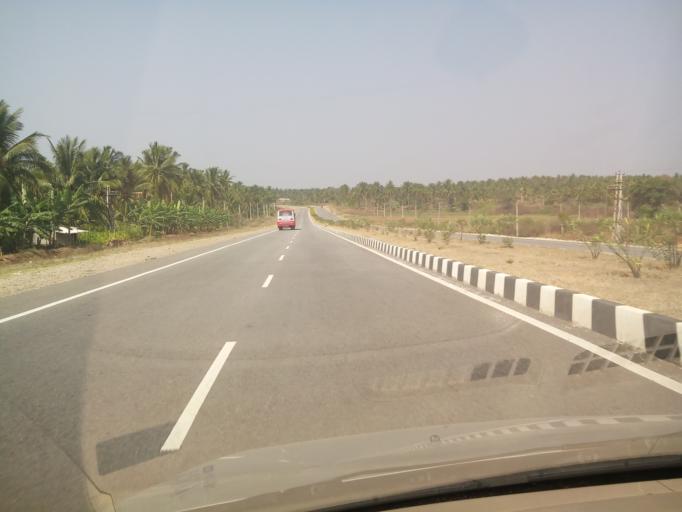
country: IN
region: Karnataka
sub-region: Hassan
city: Shravanabelagola
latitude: 12.9166
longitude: 76.4623
